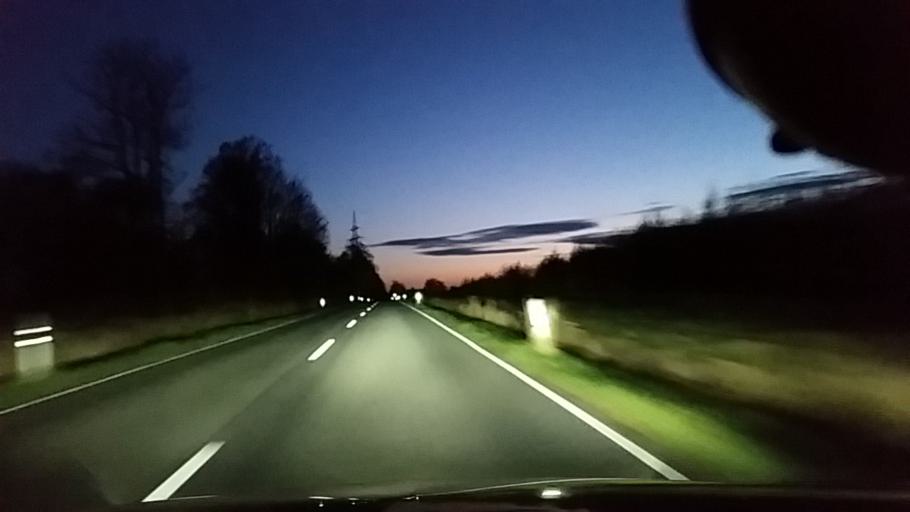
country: DE
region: Lower Saxony
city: Tappenbeck
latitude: 52.4646
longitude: 10.7593
